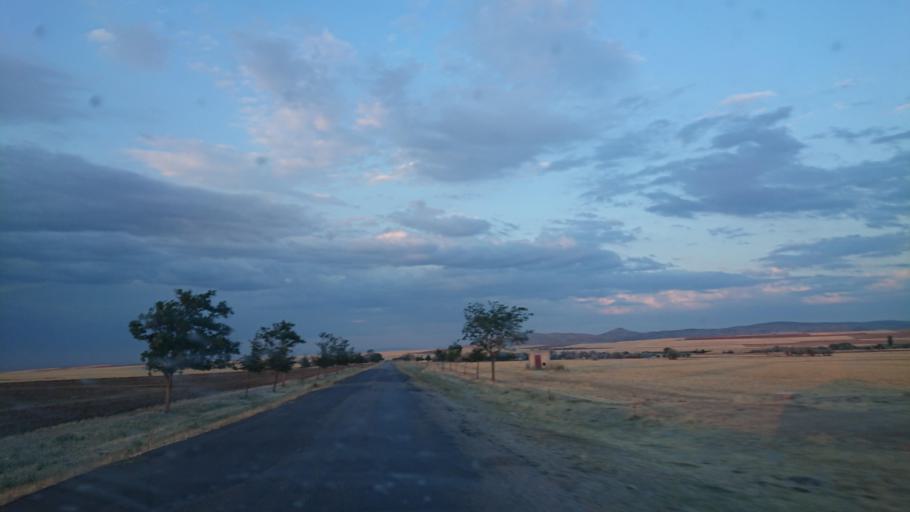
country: TR
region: Aksaray
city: Balci
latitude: 38.8251
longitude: 34.1123
